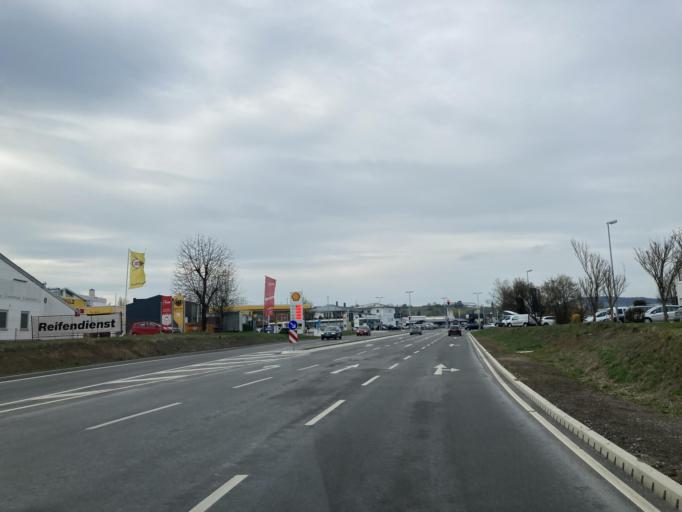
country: DE
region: Baden-Wuerttemberg
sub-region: Tuebingen Region
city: Rottenburg
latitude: 48.4788
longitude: 8.9514
